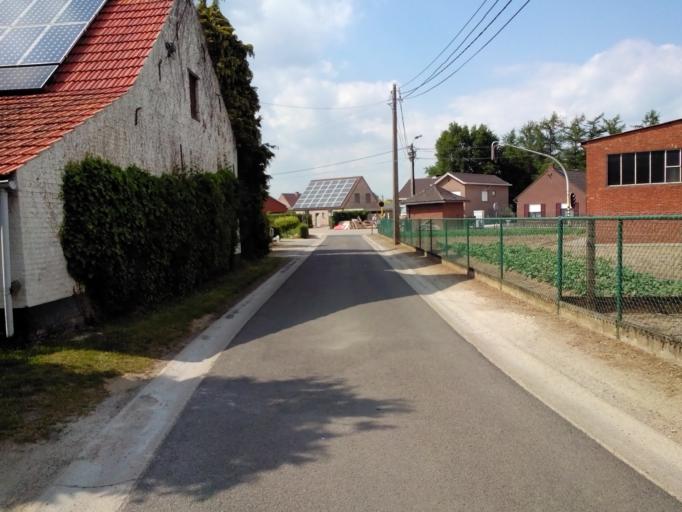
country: BE
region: Flanders
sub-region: Provincie Vlaams-Brabant
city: Tremelo
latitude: 50.9742
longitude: 4.7183
